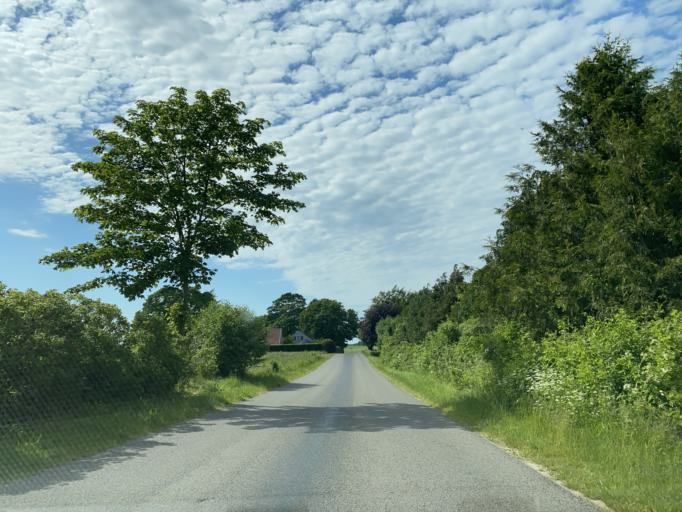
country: DK
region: Central Jutland
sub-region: Skanderborg Kommune
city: Galten
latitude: 56.2076
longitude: 9.9054
